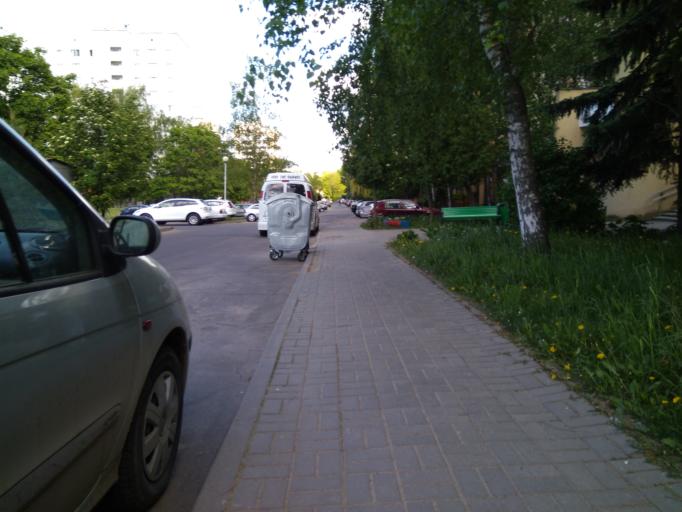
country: BY
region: Minsk
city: Minsk
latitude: 53.9085
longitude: 27.5334
